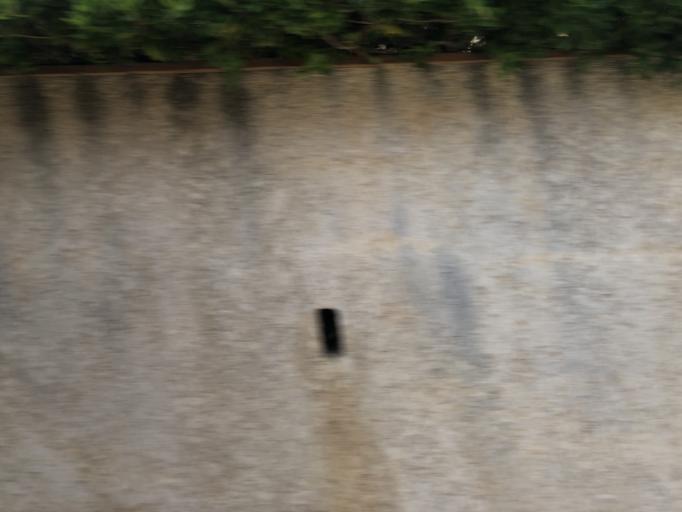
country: FR
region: Provence-Alpes-Cote d'Azur
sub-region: Departement des Alpes-Maritimes
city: Beaulieu-sur-Mer
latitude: 43.7109
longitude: 7.3291
